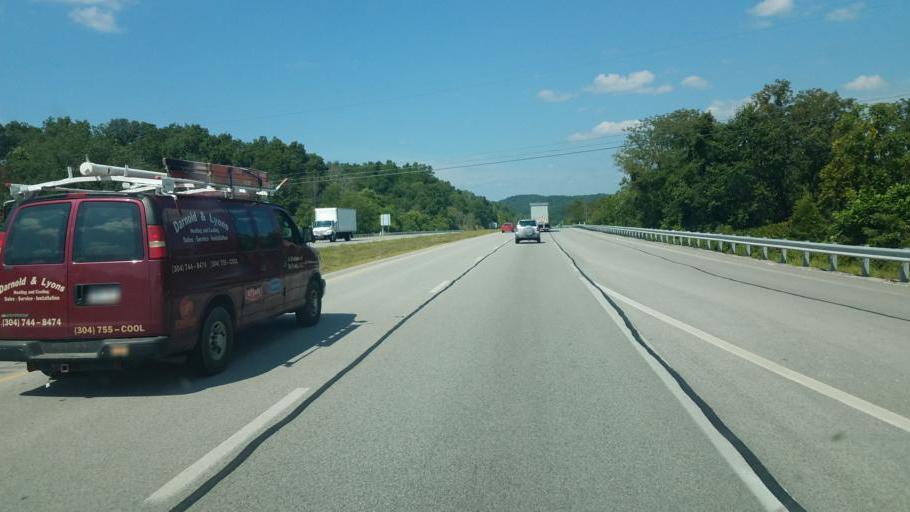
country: US
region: West Virginia
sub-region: Kanawha County
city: Sissonville
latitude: 38.6687
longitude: -81.6486
